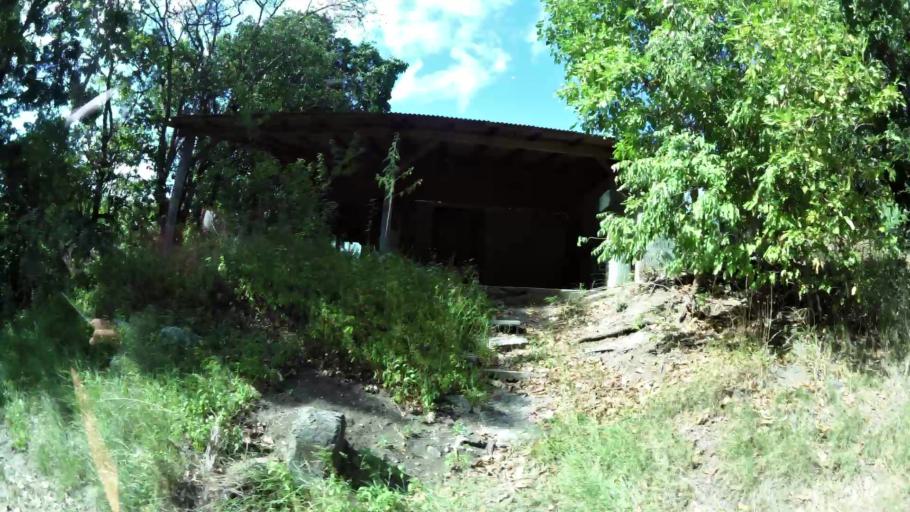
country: GP
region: Guadeloupe
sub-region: Guadeloupe
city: Sainte-Rose
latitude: 16.3360
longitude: -61.7862
